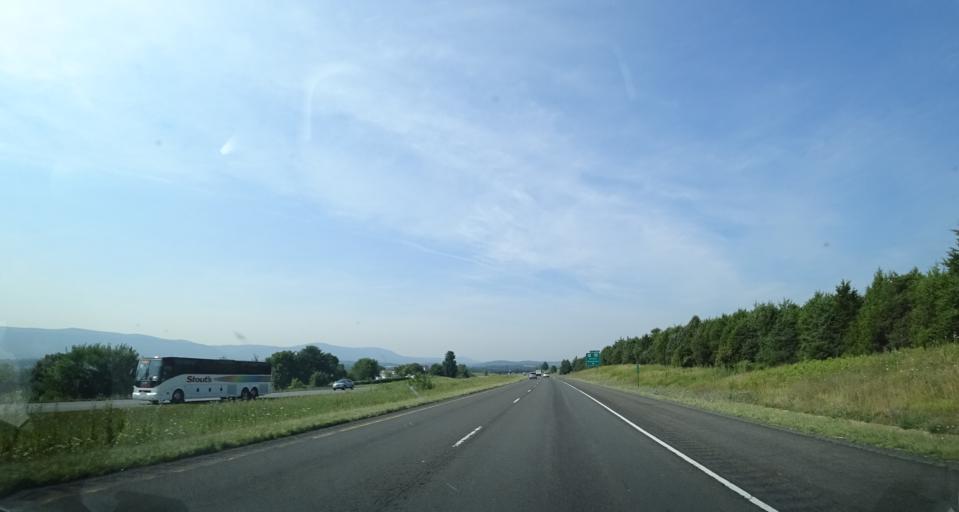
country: US
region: Virginia
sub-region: Rockingham County
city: Broadway
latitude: 38.5702
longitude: -78.7426
